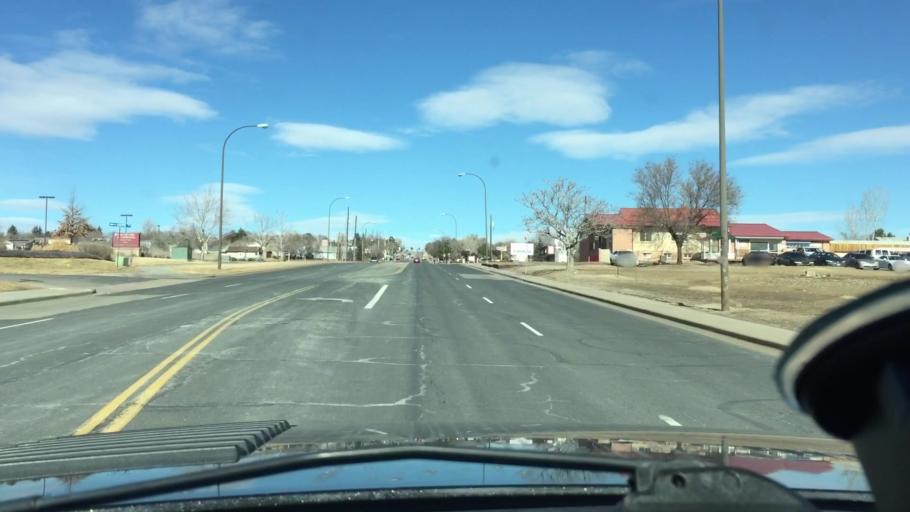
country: US
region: Colorado
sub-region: Adams County
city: Federal Heights
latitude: 39.8672
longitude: -104.9966
